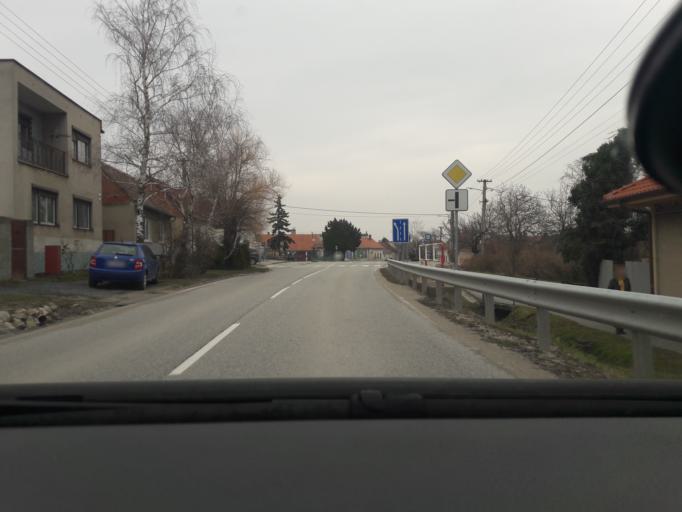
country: SK
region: Trnavsky
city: Smolenice
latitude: 48.5087
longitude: 17.4328
